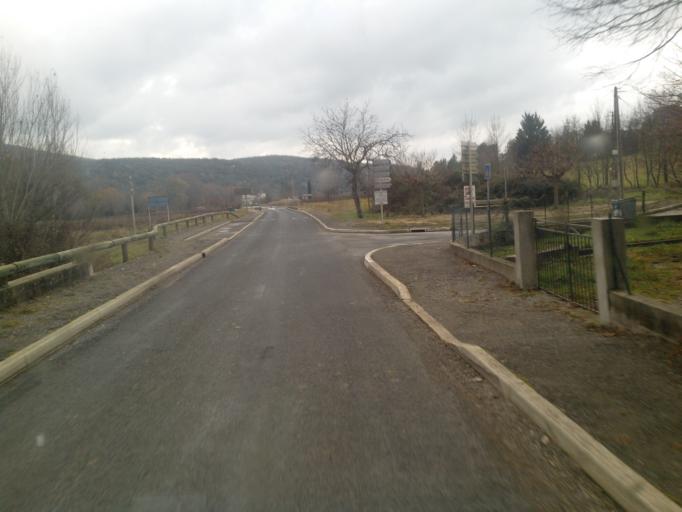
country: FR
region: Languedoc-Roussillon
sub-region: Departement de l'Herault
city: Saint-Bauzille-de-Putois
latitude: 43.9280
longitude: 3.7941
